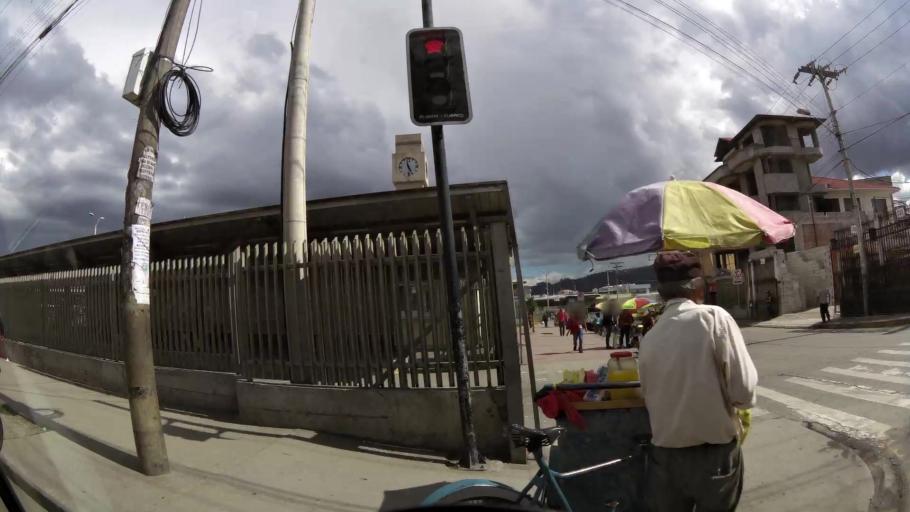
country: EC
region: Azuay
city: Cuenca
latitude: -2.8915
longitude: -78.9938
